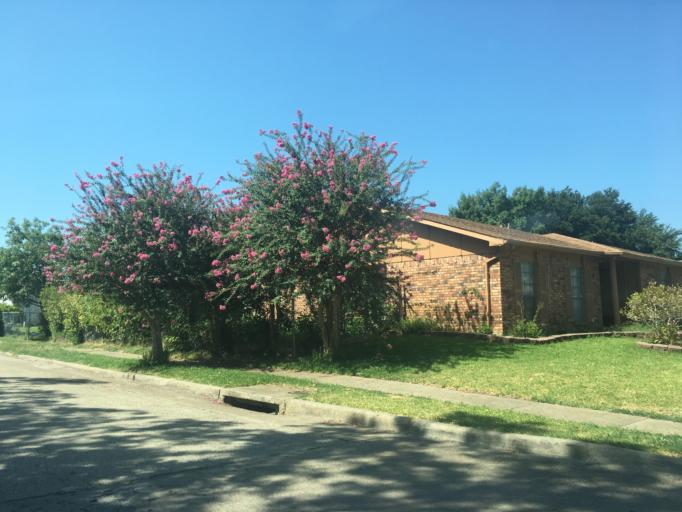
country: US
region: Texas
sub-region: Dallas County
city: Garland
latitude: 32.8523
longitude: -96.6600
